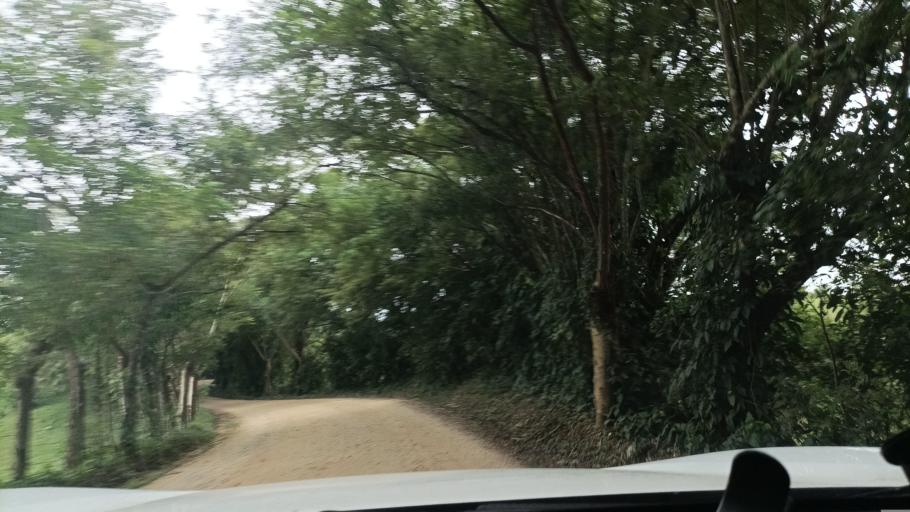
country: MX
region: Veracruz
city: Hidalgotitlan
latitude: 17.6086
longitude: -94.5242
